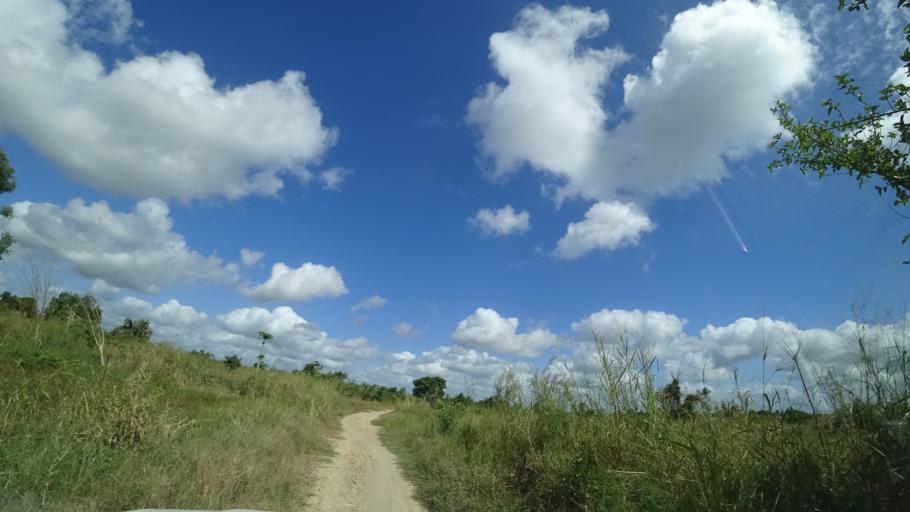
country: MZ
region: Sofala
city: Dondo
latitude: -19.3570
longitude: 34.5834
